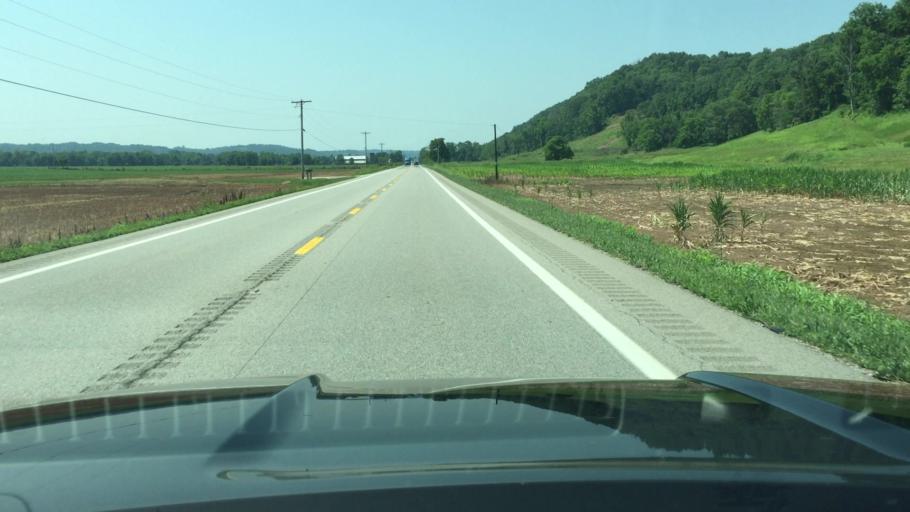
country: US
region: West Virginia
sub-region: Putnam County
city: Buffalo
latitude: 38.6667
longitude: -81.9675
